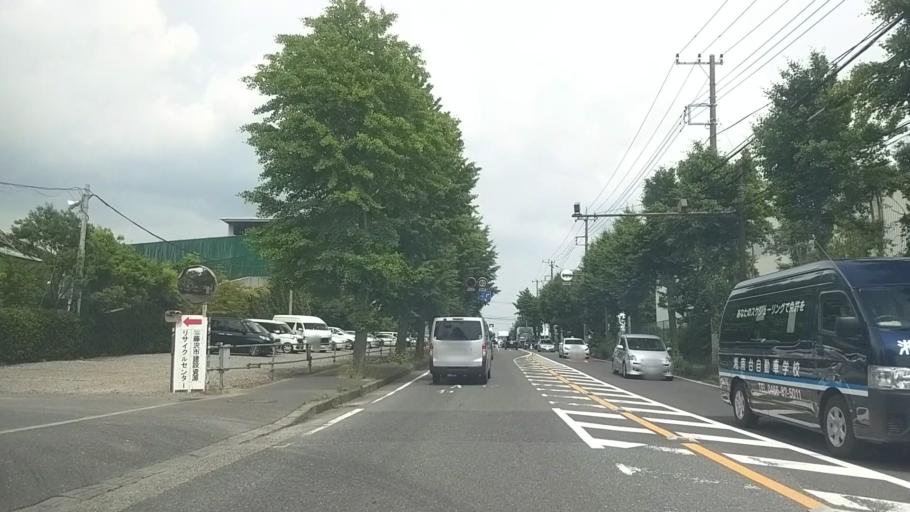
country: JP
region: Kanagawa
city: Fujisawa
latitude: 35.3946
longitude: 139.4525
